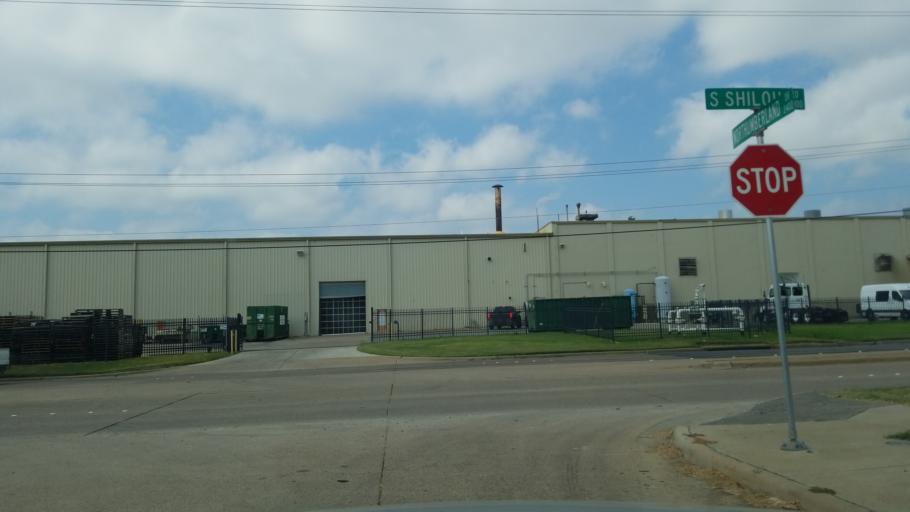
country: US
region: Texas
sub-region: Dallas County
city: Garland
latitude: 32.8929
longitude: -96.6654
